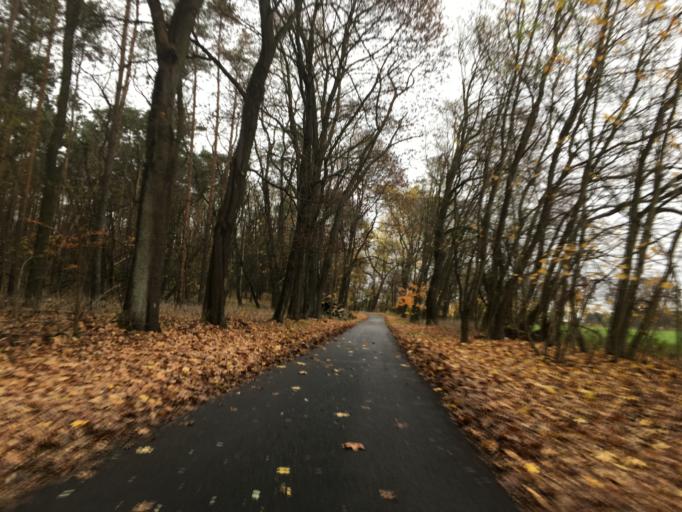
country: DE
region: Brandenburg
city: Gross Lindow
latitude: 52.2908
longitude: 14.5197
